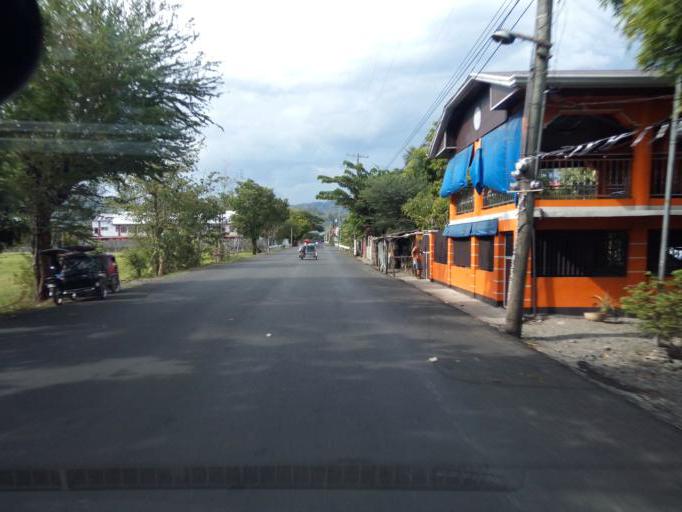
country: PH
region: Central Luzon
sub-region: Province of Nueva Ecija
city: Sibul
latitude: 15.8181
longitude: 121.0064
